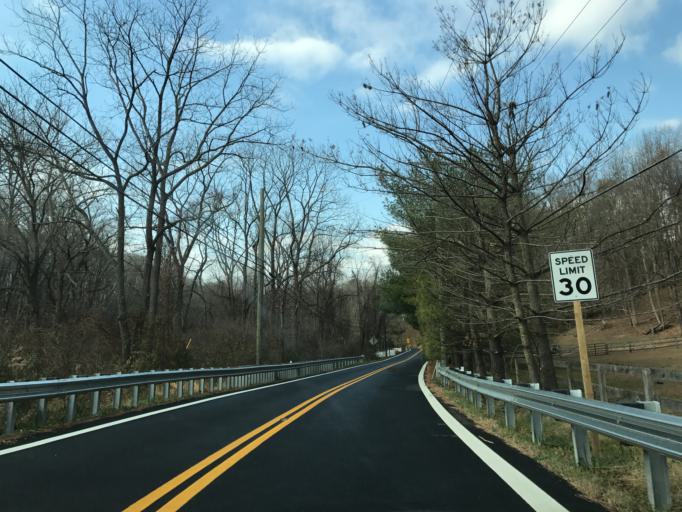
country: US
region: Maryland
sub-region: Baltimore County
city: Hunt Valley
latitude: 39.5798
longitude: -76.6033
